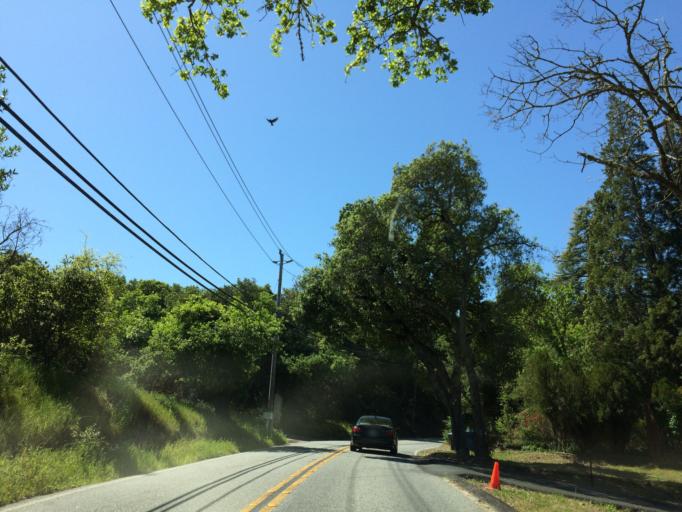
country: US
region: California
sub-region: Santa Clara County
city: Lexington Hills
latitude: 37.1873
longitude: -121.9955
